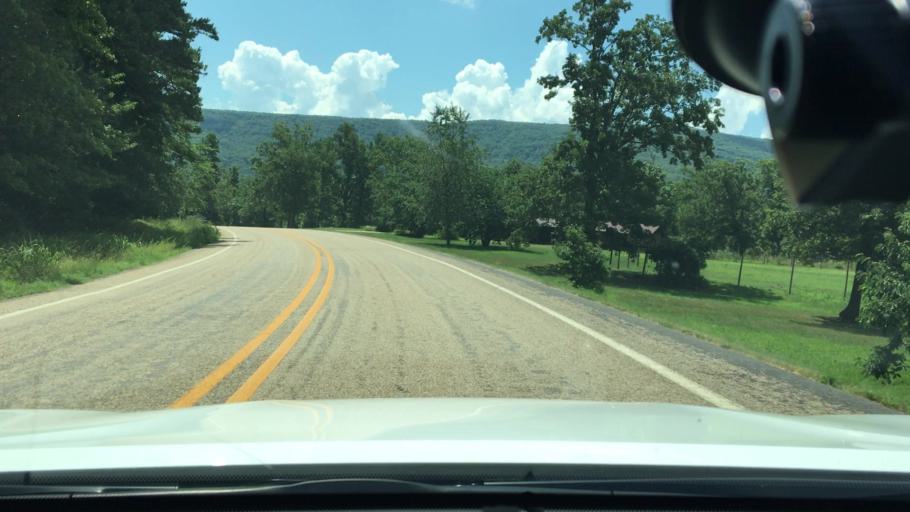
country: US
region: Arkansas
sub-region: Logan County
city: Paris
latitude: 35.1971
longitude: -93.6346
